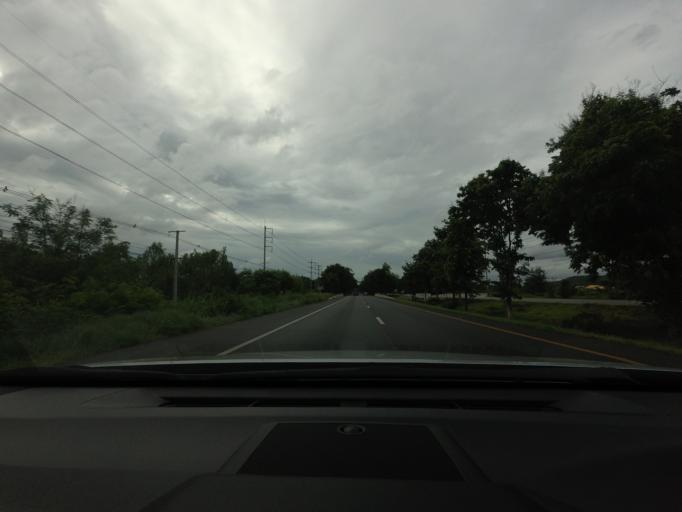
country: TH
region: Prachuap Khiri Khan
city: Hua Hin
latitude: 12.5998
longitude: 99.8626
